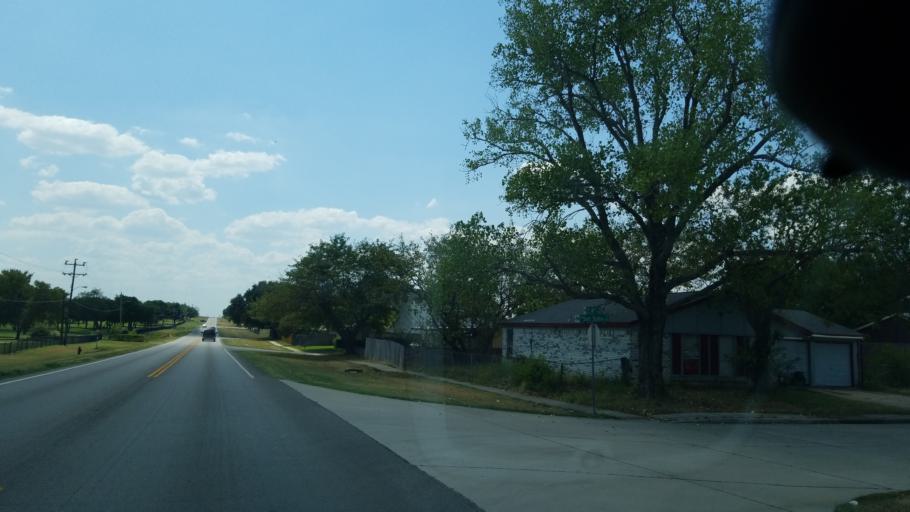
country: US
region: Texas
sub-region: Dallas County
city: Grand Prairie
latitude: 32.7027
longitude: -96.9856
